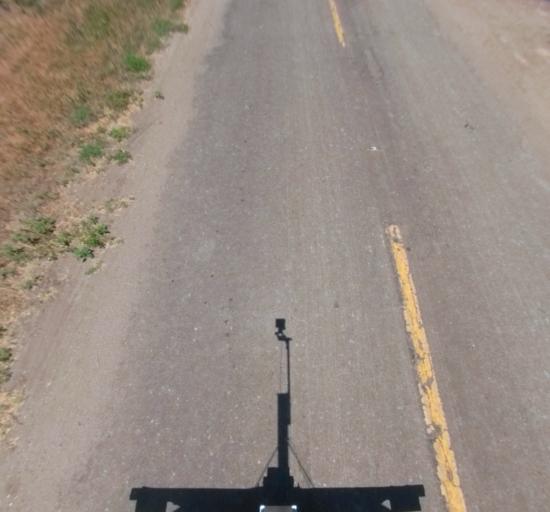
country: US
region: California
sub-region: Madera County
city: Chowchilla
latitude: 37.0127
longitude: -120.2924
